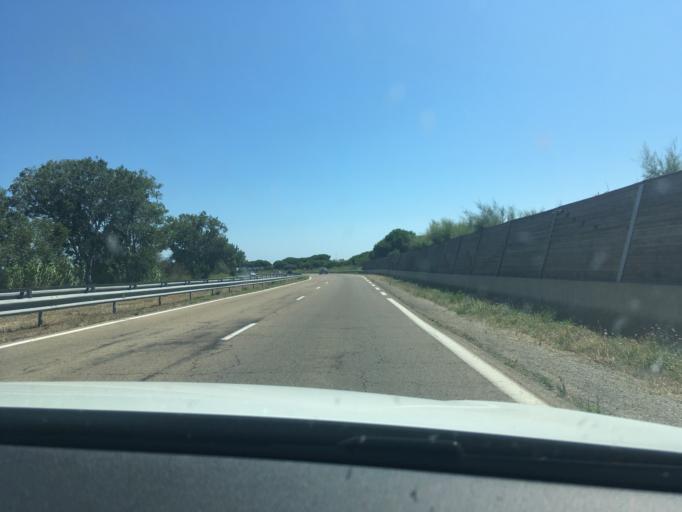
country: FR
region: Languedoc-Roussillon
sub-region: Departement du Gard
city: Le Grau-du-Roi
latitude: 43.5469
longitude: 4.1341
